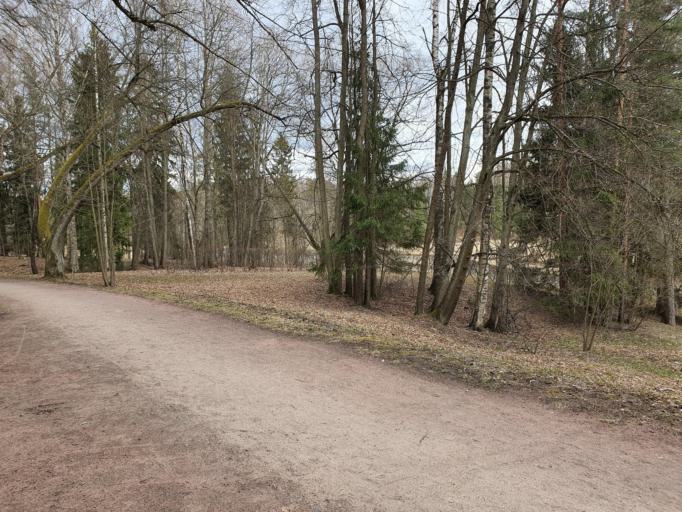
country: RU
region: St.-Petersburg
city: Tyarlevo
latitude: 59.6932
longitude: 30.4582
